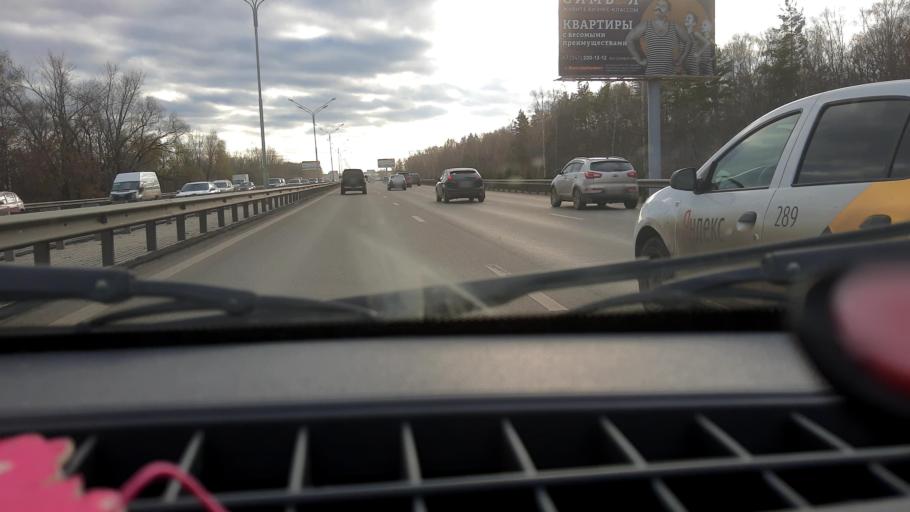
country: RU
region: Bashkortostan
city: Ufa
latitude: 54.6901
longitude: 55.9388
